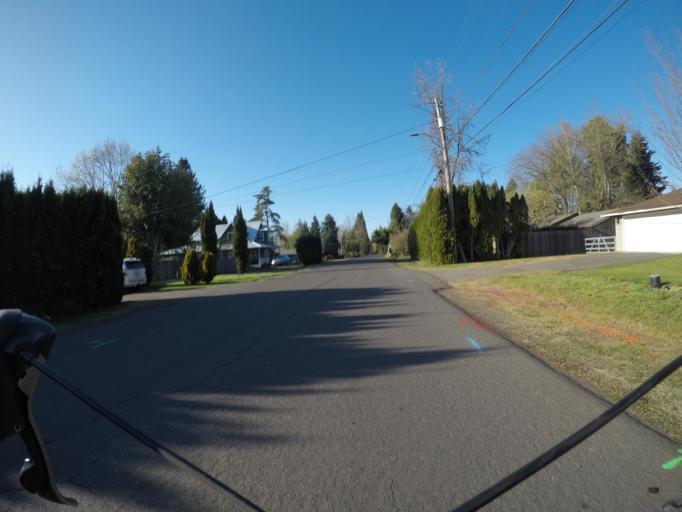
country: US
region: Oregon
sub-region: Washington County
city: Aloha
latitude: 45.4800
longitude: -122.8751
